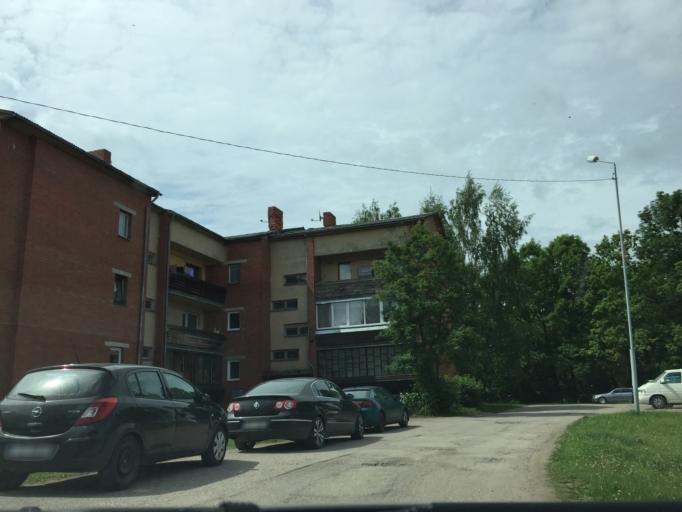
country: LV
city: Tireli
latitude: 56.6887
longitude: 23.5011
